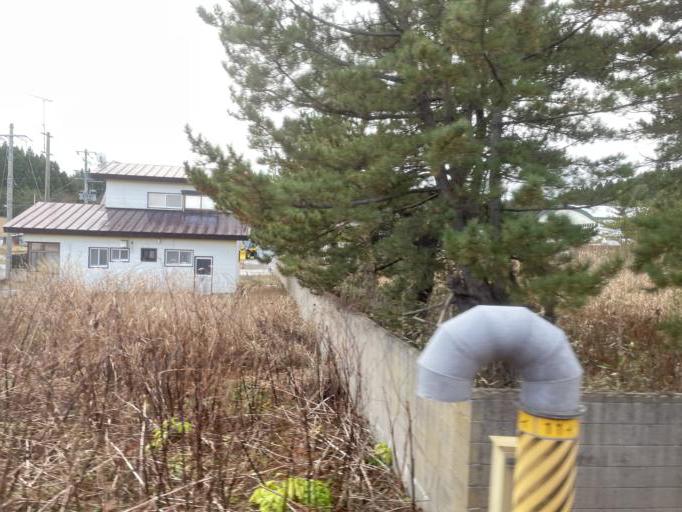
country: JP
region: Aomori
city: Aomori Shi
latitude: 41.0367
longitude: 140.6443
